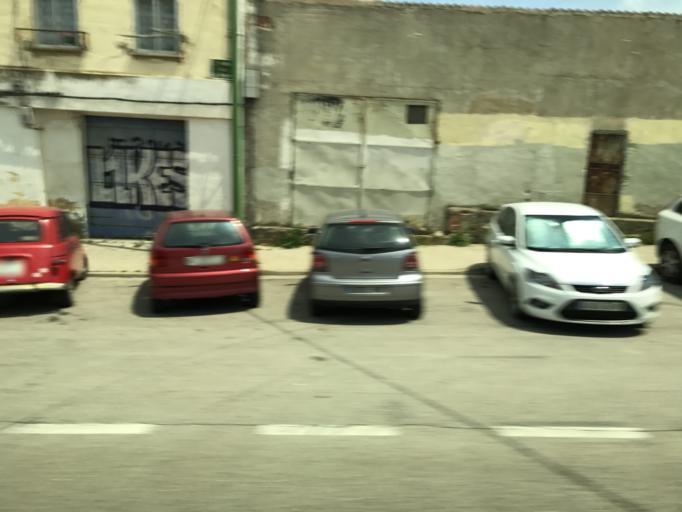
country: ES
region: Castille and Leon
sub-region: Provincia de Burgos
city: Burgos
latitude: 42.3254
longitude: -3.7013
